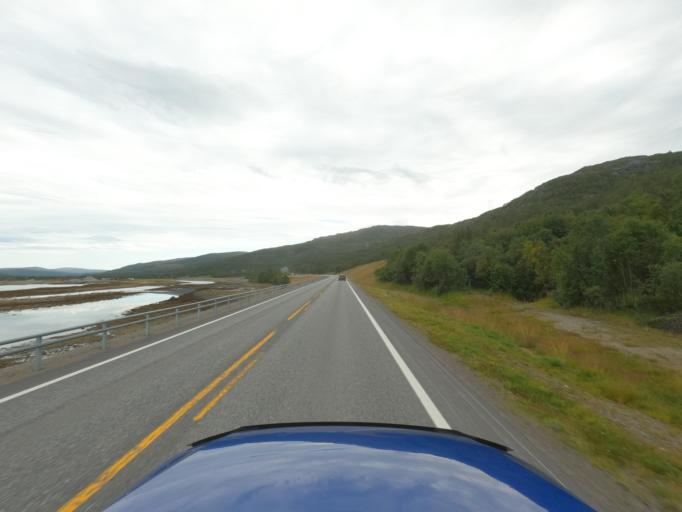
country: NO
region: Finnmark Fylke
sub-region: Kvalsund
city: Kvalsund
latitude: 70.4505
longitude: 24.2963
